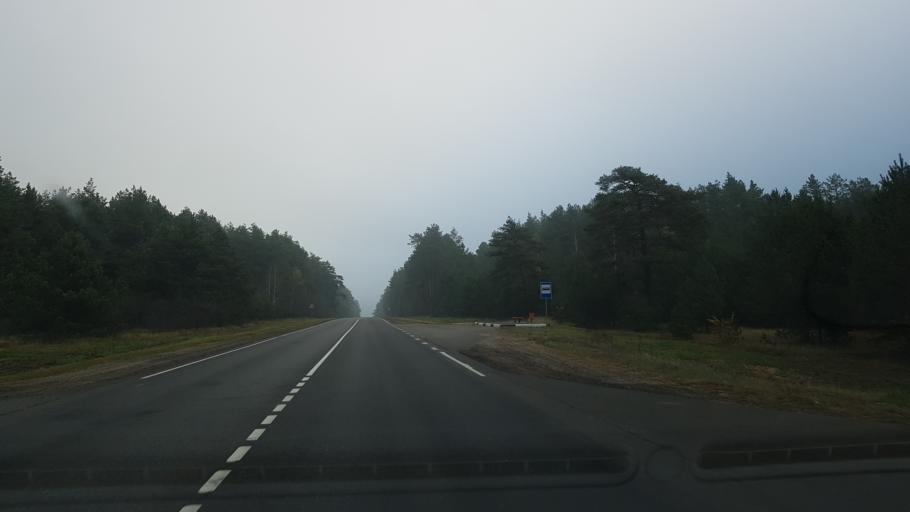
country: BY
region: Mogilev
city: Babruysk
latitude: 53.1615
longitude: 29.3238
